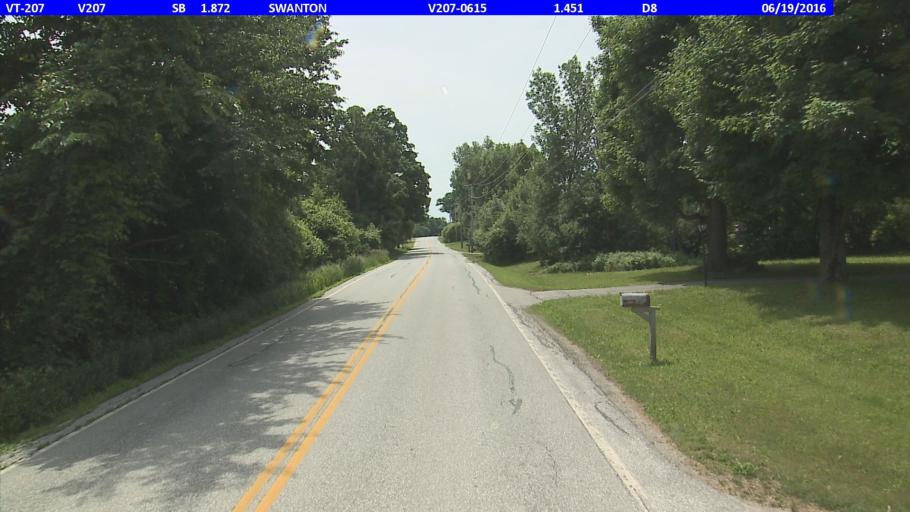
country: US
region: Vermont
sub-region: Franklin County
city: Saint Albans
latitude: 44.8659
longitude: -73.0754
